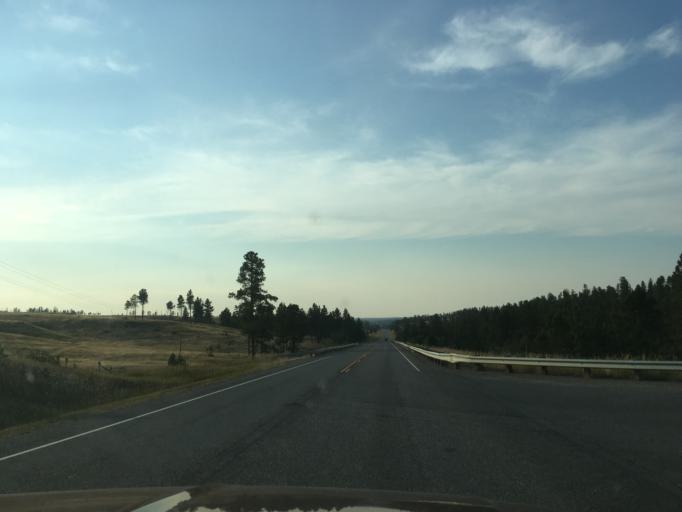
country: US
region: Montana
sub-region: Musselshell County
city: Roundup
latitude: 46.2631
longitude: -108.4673
